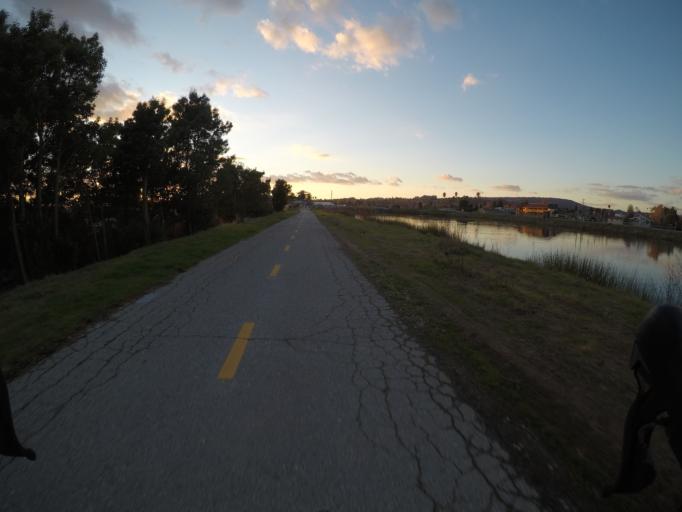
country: US
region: California
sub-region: Santa Cruz County
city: Santa Cruz
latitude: 36.9676
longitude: -122.0151
